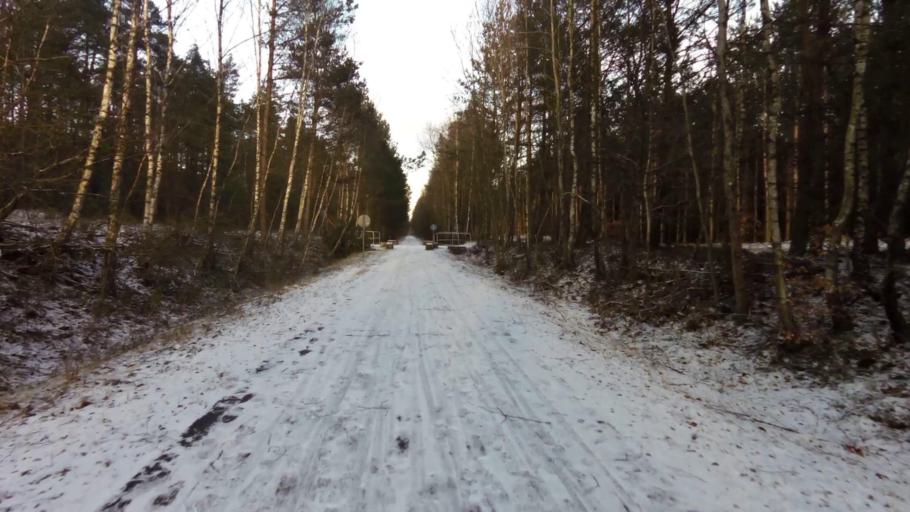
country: PL
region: West Pomeranian Voivodeship
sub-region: Powiat drawski
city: Zlocieniec
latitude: 53.5573
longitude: 16.0278
